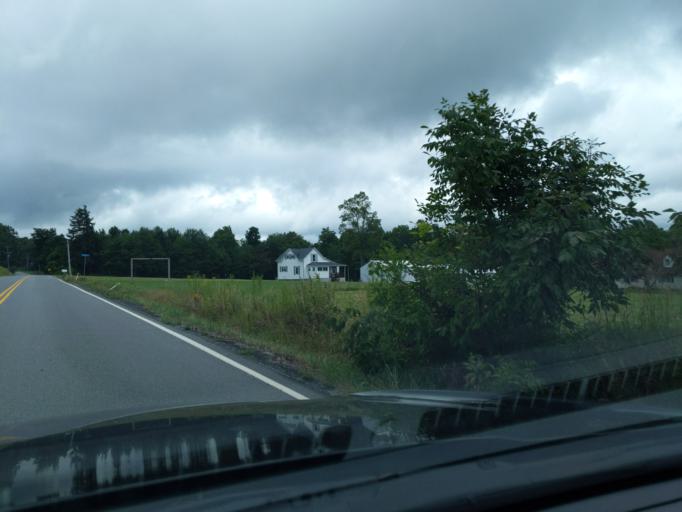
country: US
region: Pennsylvania
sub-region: Blair County
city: Claysburg
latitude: 40.3422
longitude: -78.5566
